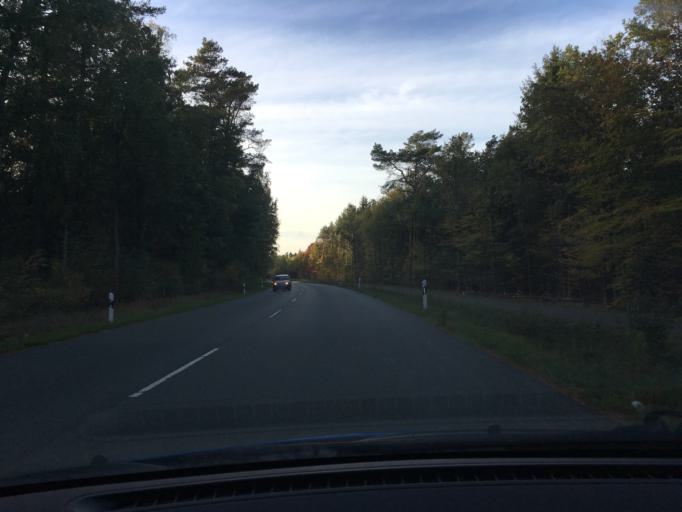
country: DE
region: Lower Saxony
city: Munster
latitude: 53.0436
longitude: 10.0570
